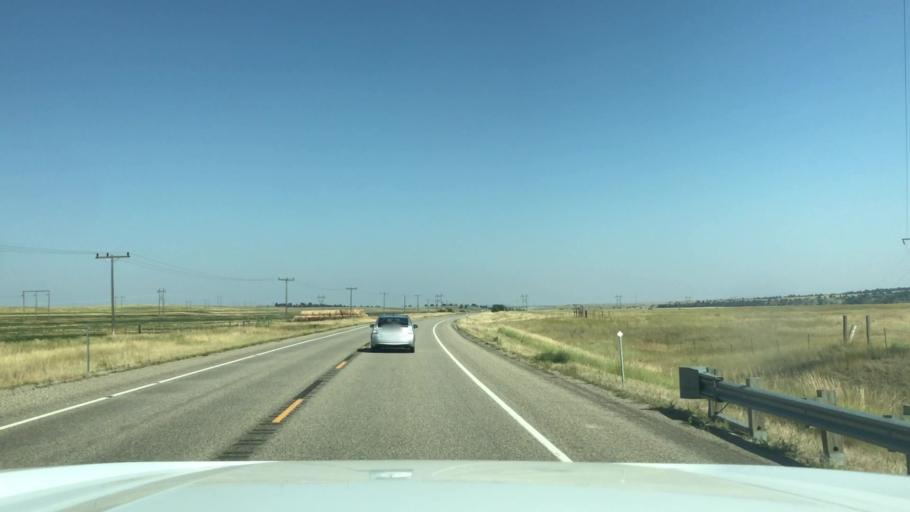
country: US
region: Montana
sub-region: Golden Valley County
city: Ryegate
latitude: 46.3283
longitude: -109.4702
